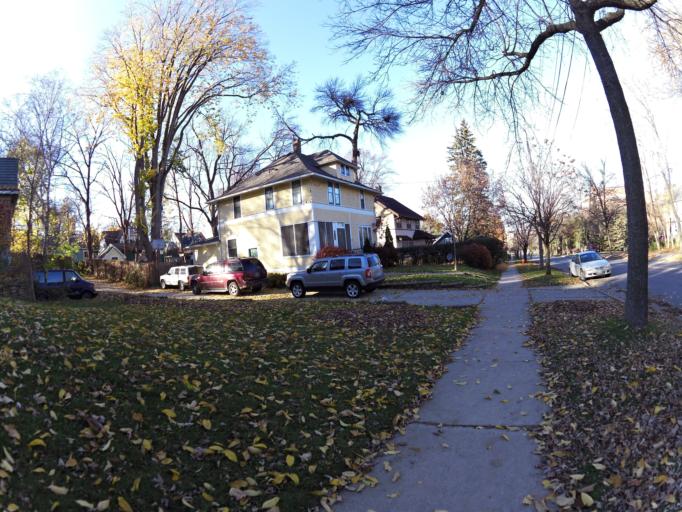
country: US
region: Minnesota
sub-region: Olmsted County
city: Rochester
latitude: 44.0175
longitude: -92.4842
